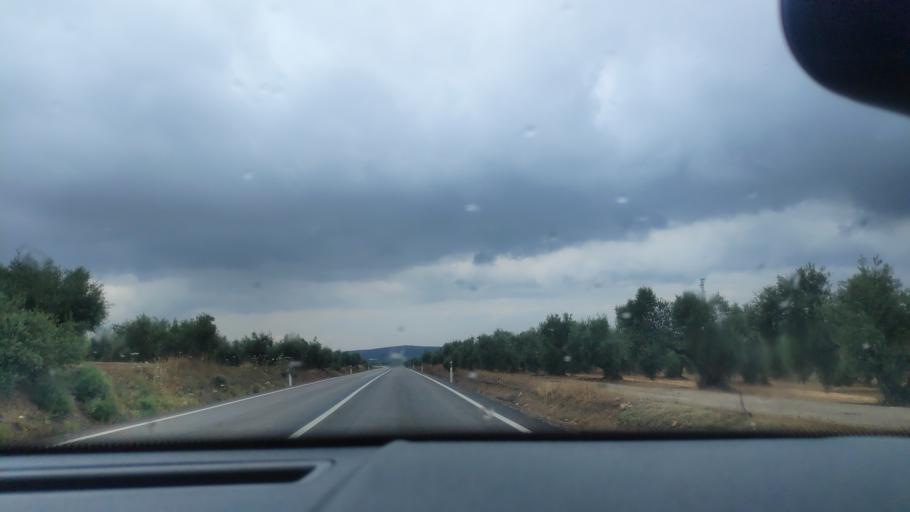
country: ES
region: Andalusia
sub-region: Provincia de Jaen
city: Jabalquinto
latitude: 38.0389
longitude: -3.7442
